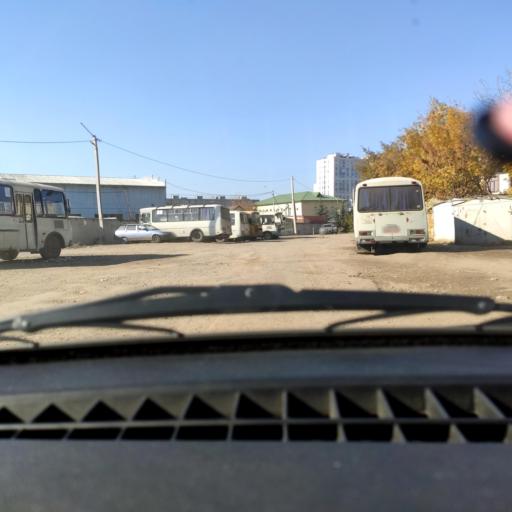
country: RU
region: Bashkortostan
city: Ufa
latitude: 54.7734
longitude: 56.1274
